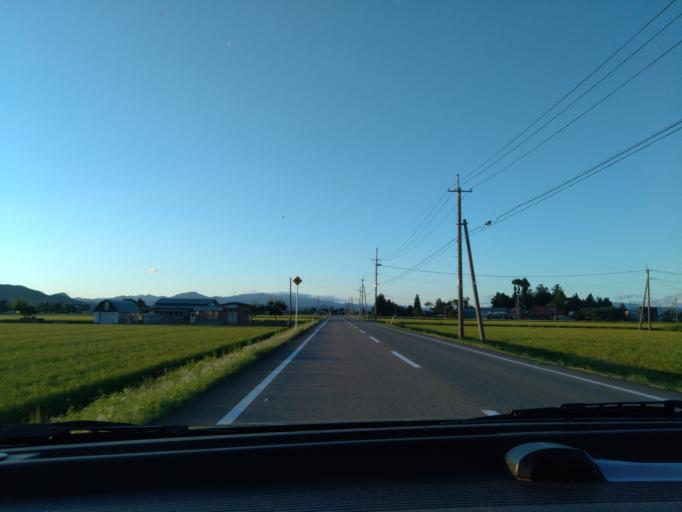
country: JP
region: Akita
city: Kakunodatemachi
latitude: 39.5125
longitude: 140.5588
